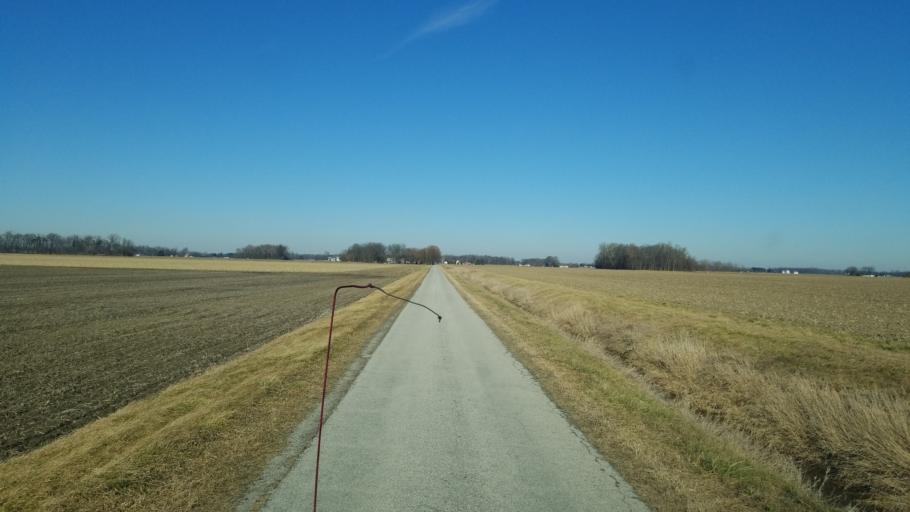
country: US
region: Ohio
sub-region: Henry County
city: Liberty Center
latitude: 41.3591
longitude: -83.9802
